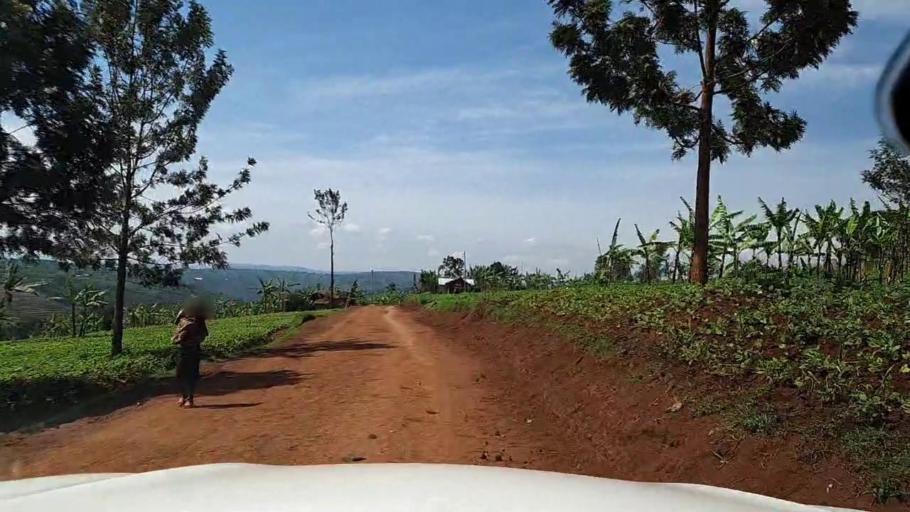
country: RW
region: Southern Province
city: Butare
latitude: -2.7033
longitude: 29.8456
